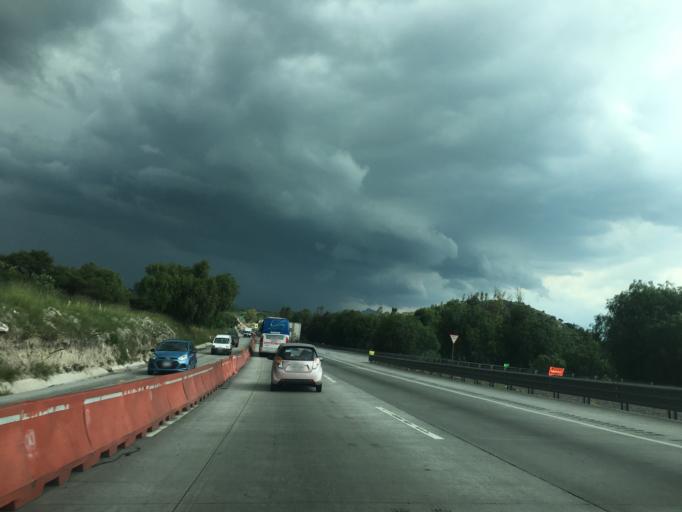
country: MX
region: Hidalgo
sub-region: Tepeji del Rio de Ocampo
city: Santiago Tlapanaloya
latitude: 19.8798
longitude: -99.3427
